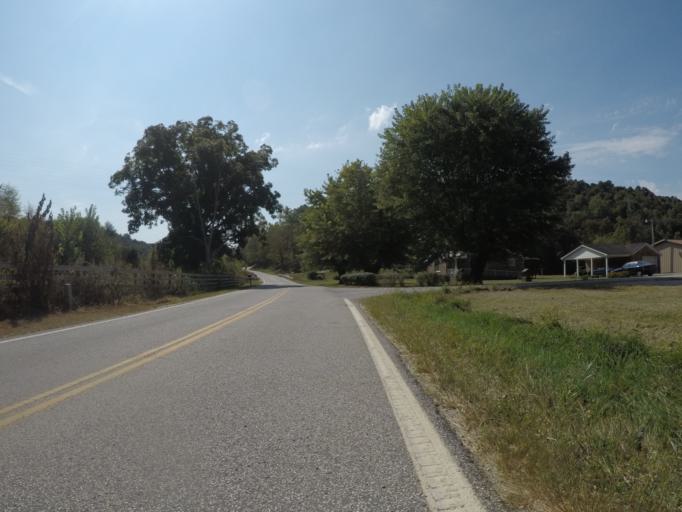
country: US
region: West Virginia
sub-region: Cabell County
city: Lesage
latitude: 38.5567
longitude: -82.3920
